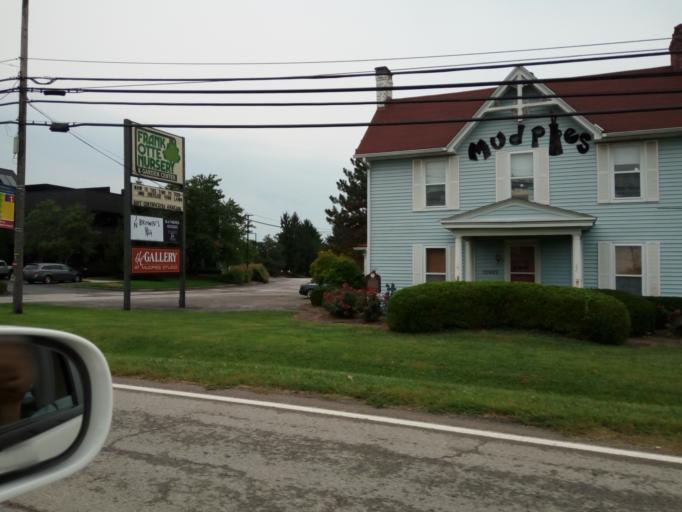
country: US
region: Kentucky
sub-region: Jefferson County
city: Middletown
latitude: 38.2432
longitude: -85.5163
